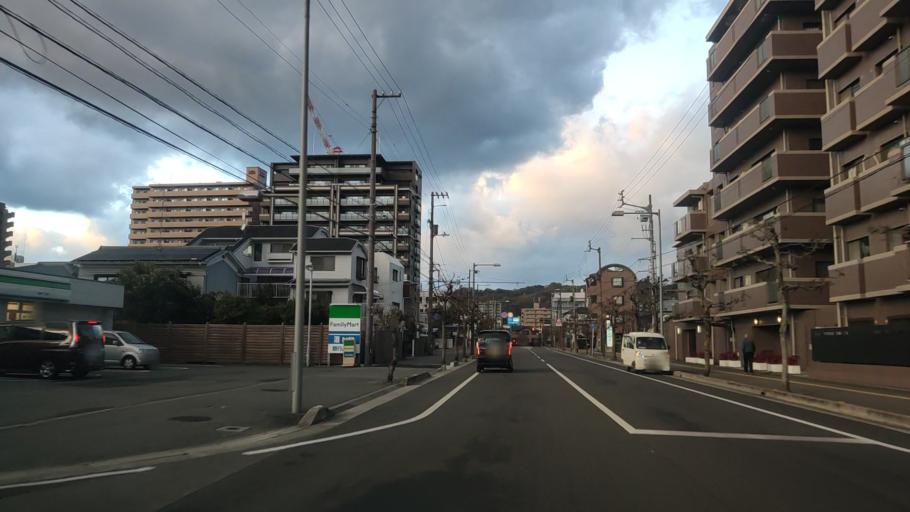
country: JP
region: Ehime
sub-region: Shikoku-chuo Shi
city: Matsuyama
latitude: 33.8455
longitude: 132.7843
